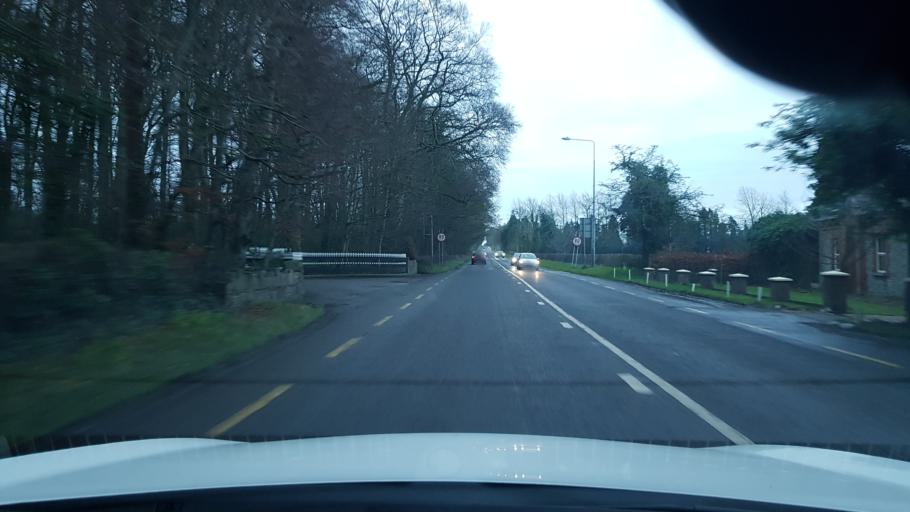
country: IE
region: Leinster
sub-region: An Mhi
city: Navan
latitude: 53.6293
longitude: -6.6576
